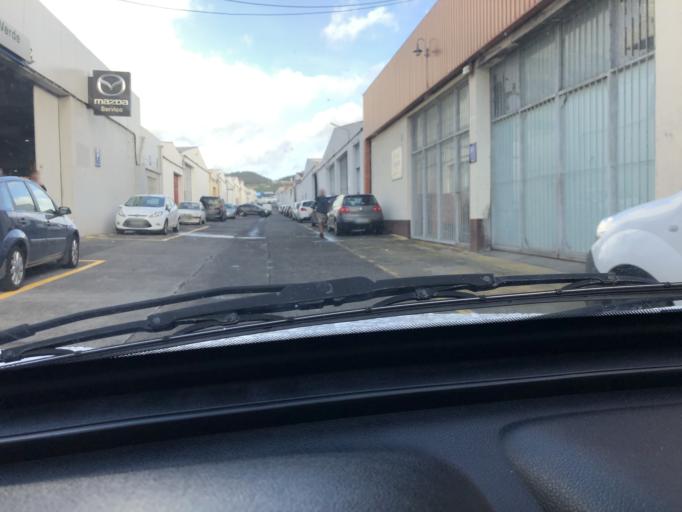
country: PT
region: Azores
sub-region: Ponta Delgada
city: Rosto de Cao
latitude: 37.7482
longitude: -25.6562
